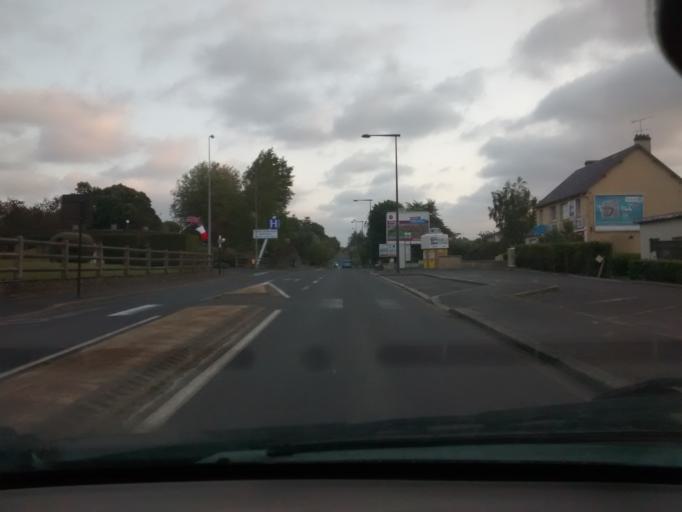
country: FR
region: Lower Normandy
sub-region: Departement de la Manche
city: Agneaux
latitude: 49.1073
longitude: -1.1080
